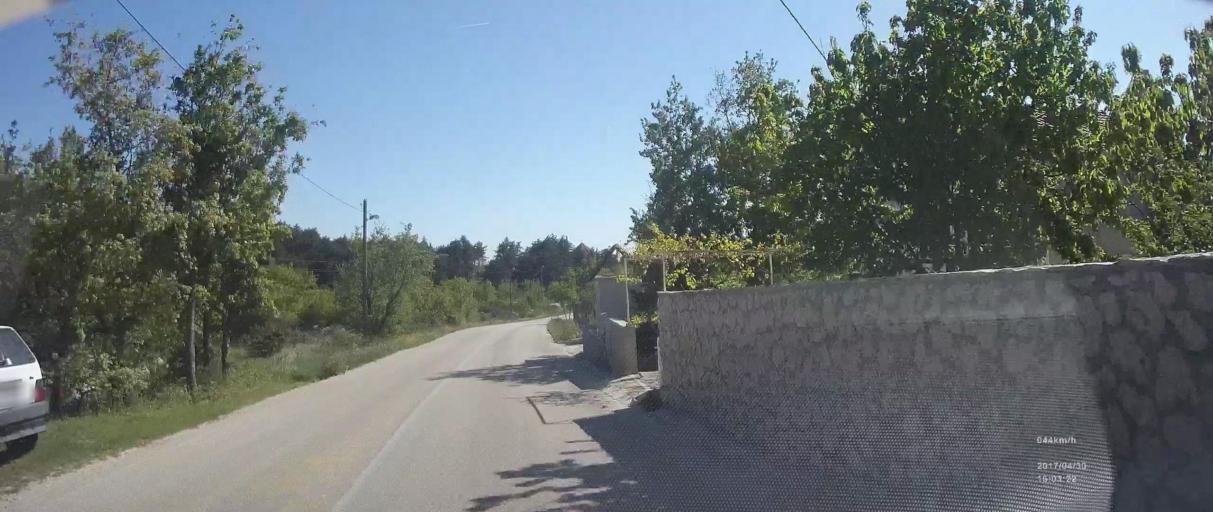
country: HR
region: Splitsko-Dalmatinska
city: Srinjine
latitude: 43.5122
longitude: 16.6068
